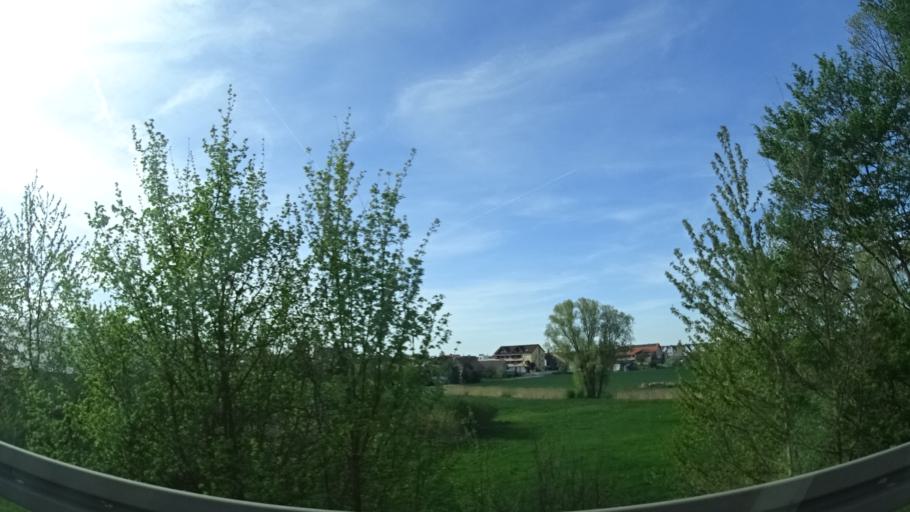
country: DE
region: Bavaria
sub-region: Regierungsbezirk Unterfranken
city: Schwebheim
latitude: 49.9509
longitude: 10.2678
